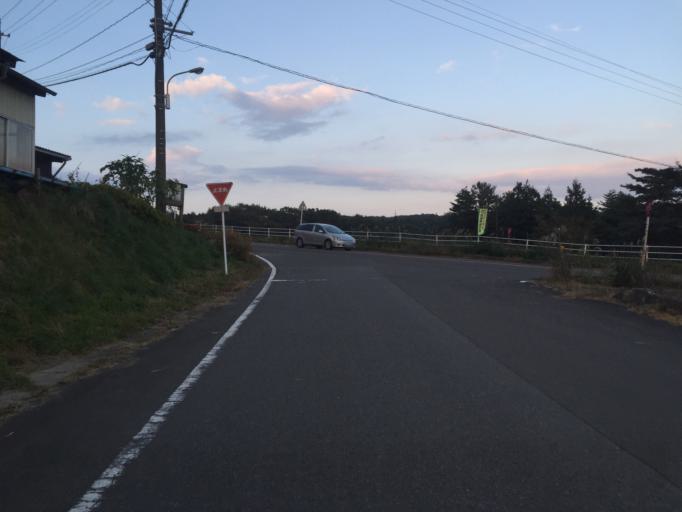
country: JP
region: Fukushima
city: Nihommatsu
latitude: 37.6137
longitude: 140.3579
